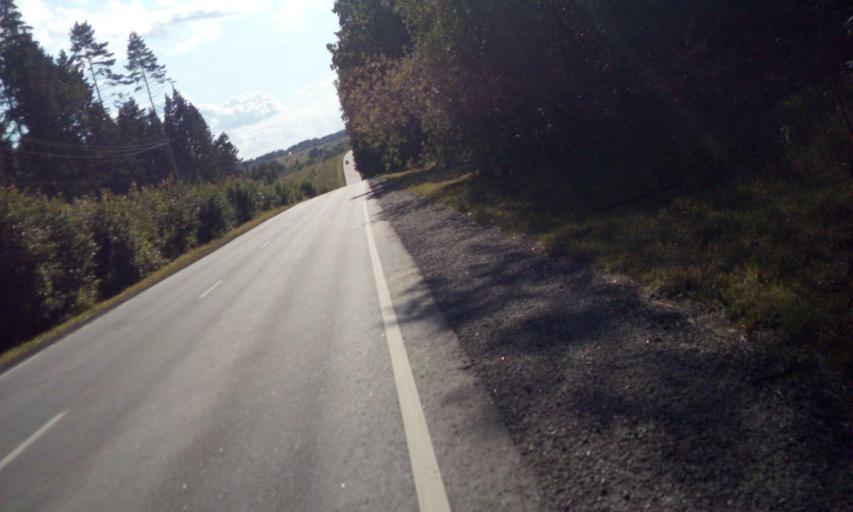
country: RU
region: Moskovskaya
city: Kievskij
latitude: 55.3156
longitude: 37.0419
